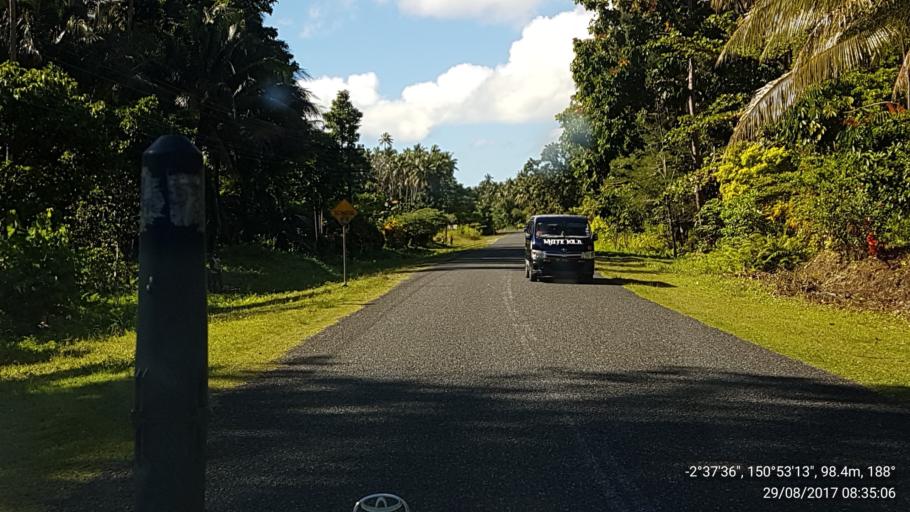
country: PG
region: New Ireland
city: Kavieng
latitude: -2.6269
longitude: 150.8872
